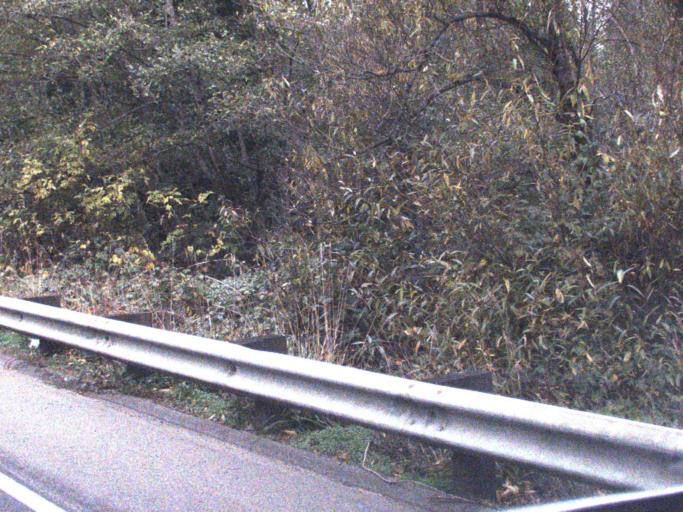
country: US
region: Washington
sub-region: Island County
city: Langley
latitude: 48.0034
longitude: -122.4321
